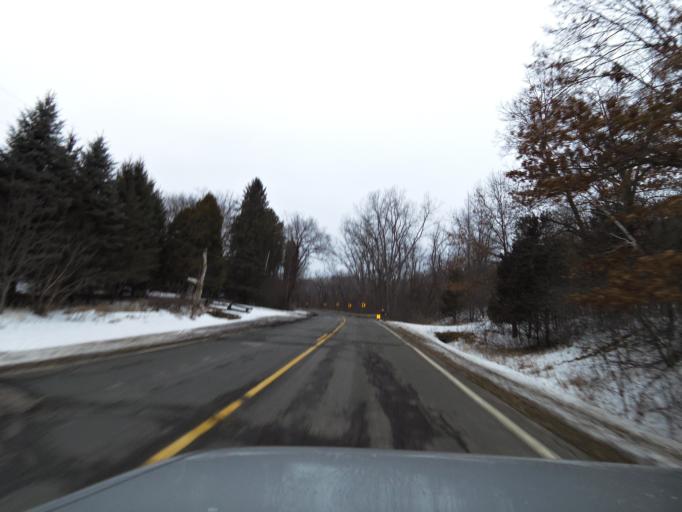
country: US
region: Minnesota
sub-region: Washington County
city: Afton
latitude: 44.8595
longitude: -92.7991
